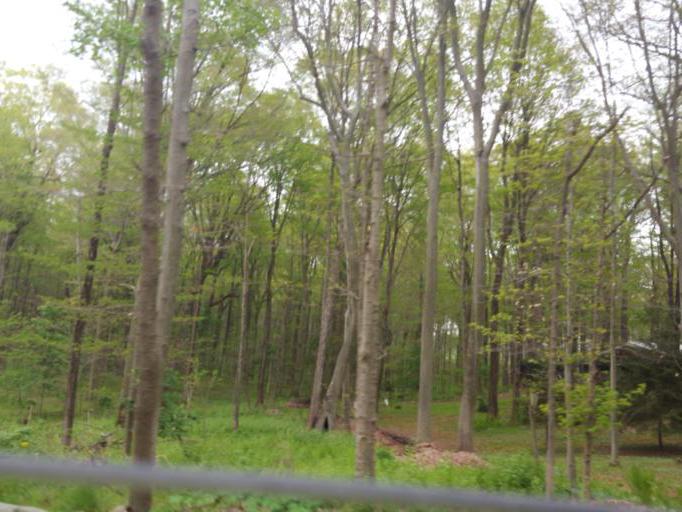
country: US
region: Ohio
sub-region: Richland County
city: Lexington
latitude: 40.7009
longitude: -82.5986
